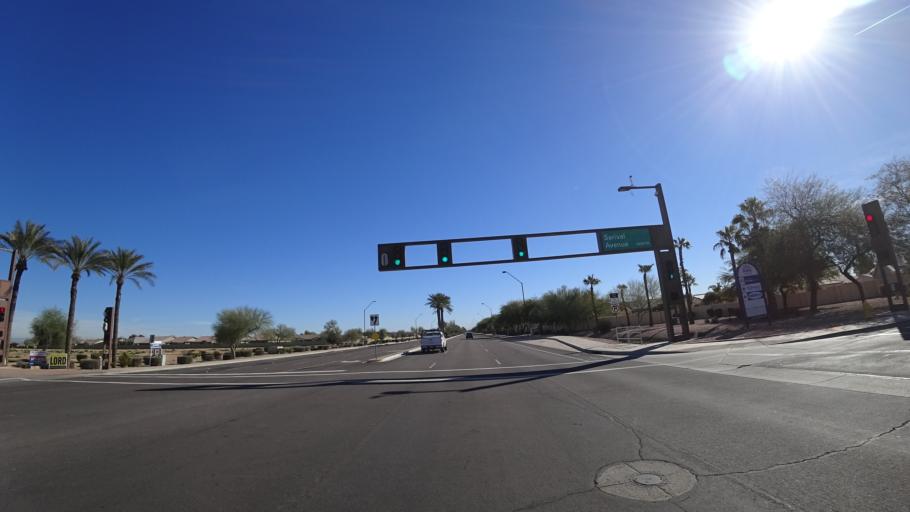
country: US
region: Arizona
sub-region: Maricopa County
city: Litchfield Park
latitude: 33.4937
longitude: -112.4097
